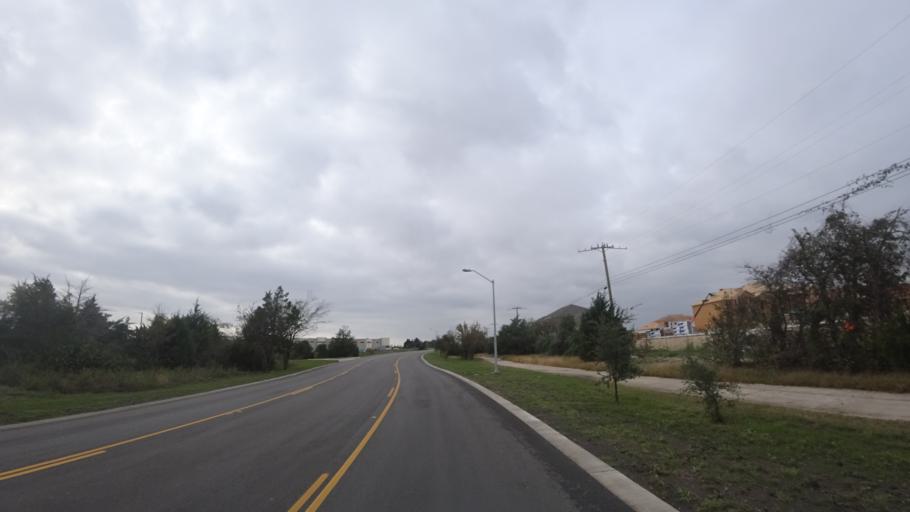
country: US
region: Texas
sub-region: Travis County
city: Pflugerville
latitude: 30.4231
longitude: -97.5921
